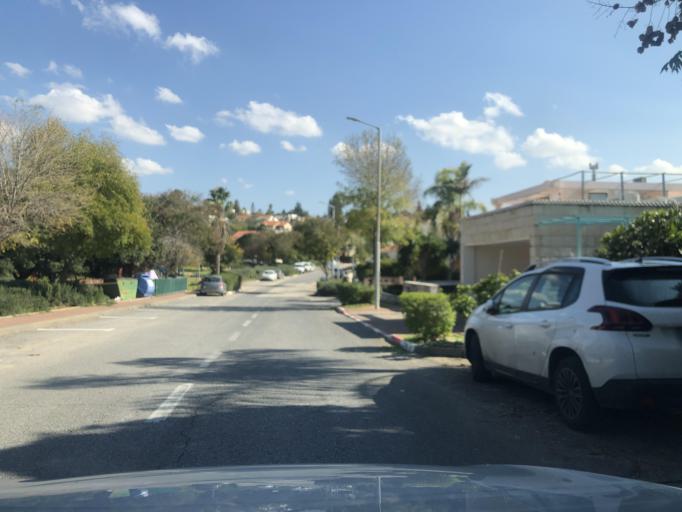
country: PS
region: West Bank
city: Azun Atme
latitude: 32.1123
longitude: 35.0277
